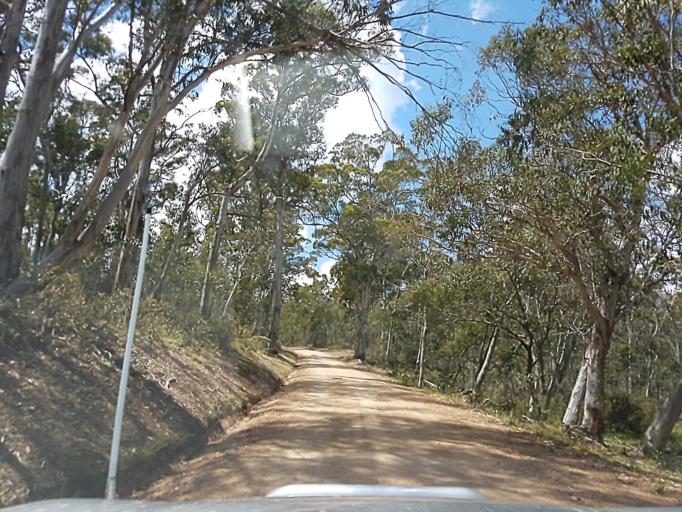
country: AU
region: New South Wales
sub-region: Snowy River
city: Jindabyne
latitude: -36.8779
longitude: 148.0781
